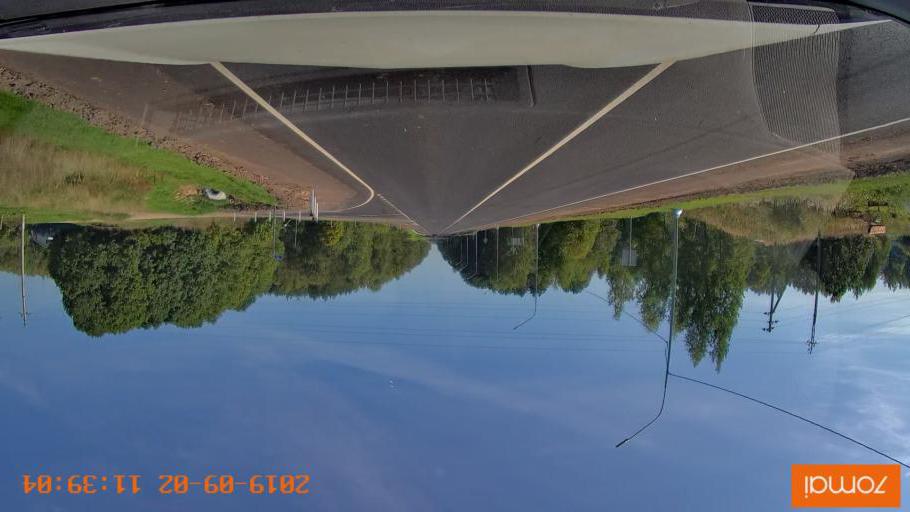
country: RU
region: Smolensk
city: Oster
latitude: 53.9100
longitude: 32.7297
